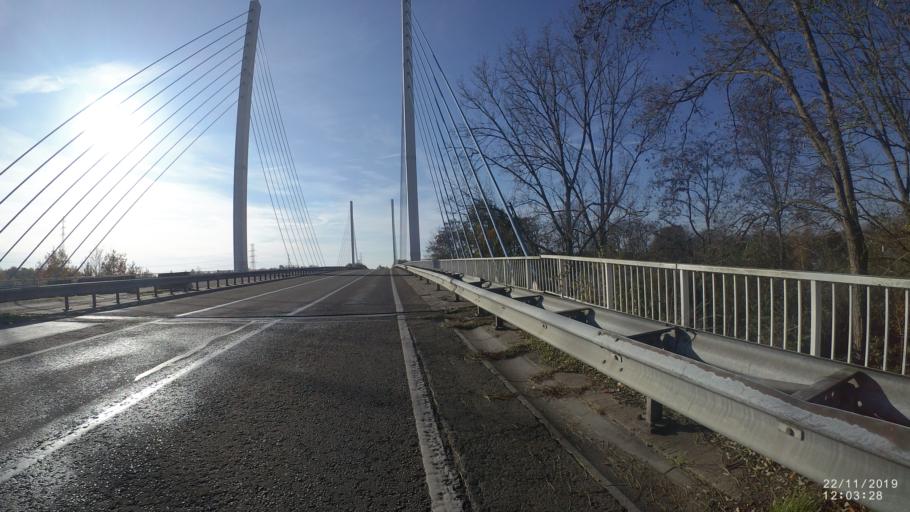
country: BE
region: Flanders
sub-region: Provincie Limburg
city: Diepenbeek
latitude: 50.9413
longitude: 5.4029
